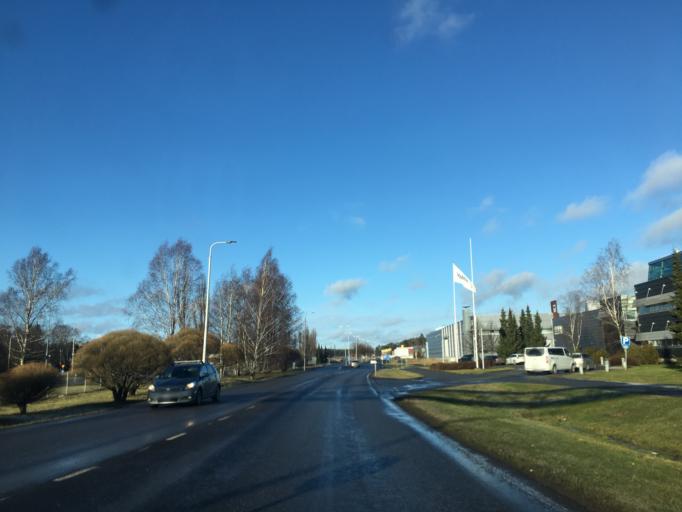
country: FI
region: Varsinais-Suomi
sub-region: Turku
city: Raisio
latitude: 60.4830
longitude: 22.1424
